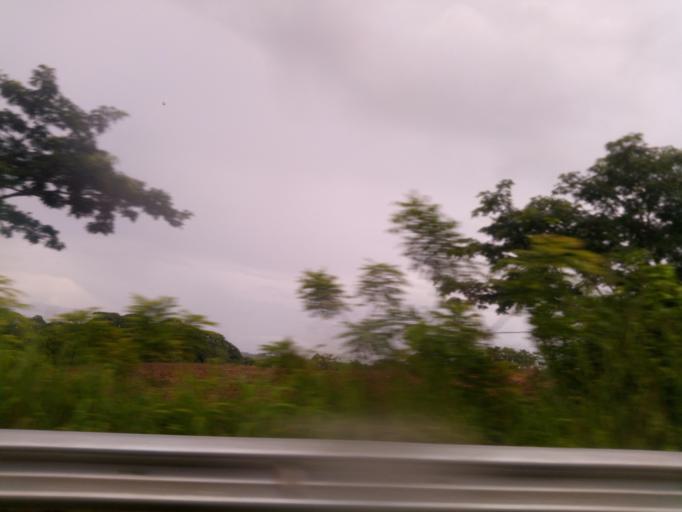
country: PA
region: Los Santos
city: Pedasi
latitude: 7.6186
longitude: -80.0858
